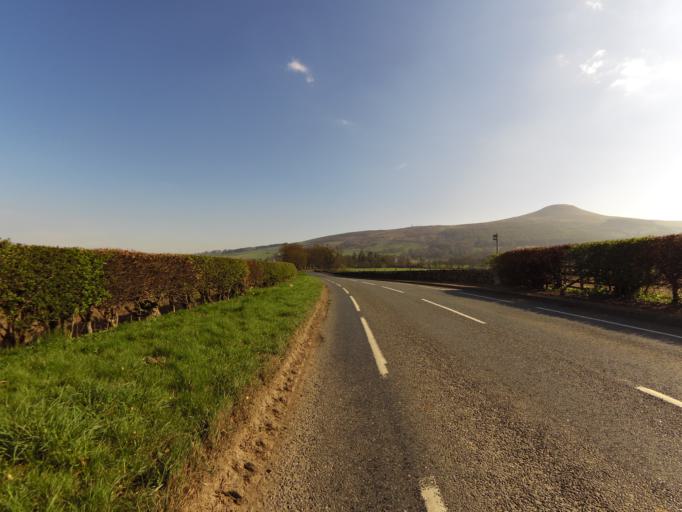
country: GB
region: Scotland
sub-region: Fife
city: Falkland
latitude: 56.2616
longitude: -3.2079
